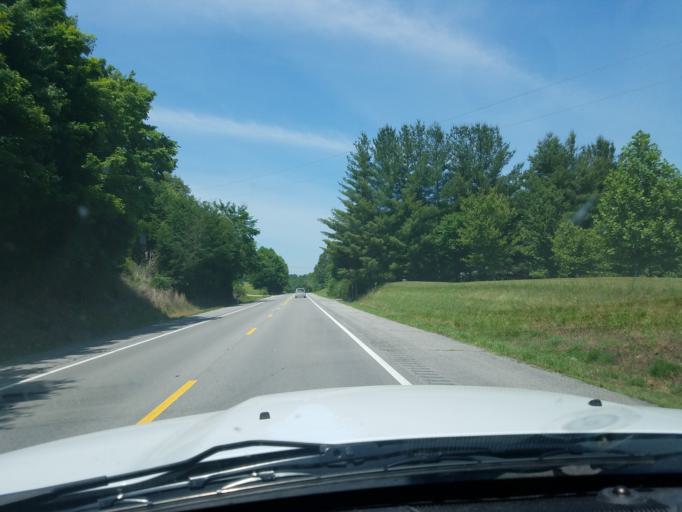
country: US
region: Tennessee
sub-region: Sumner County
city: Westmoreland
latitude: 36.5974
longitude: -86.2340
